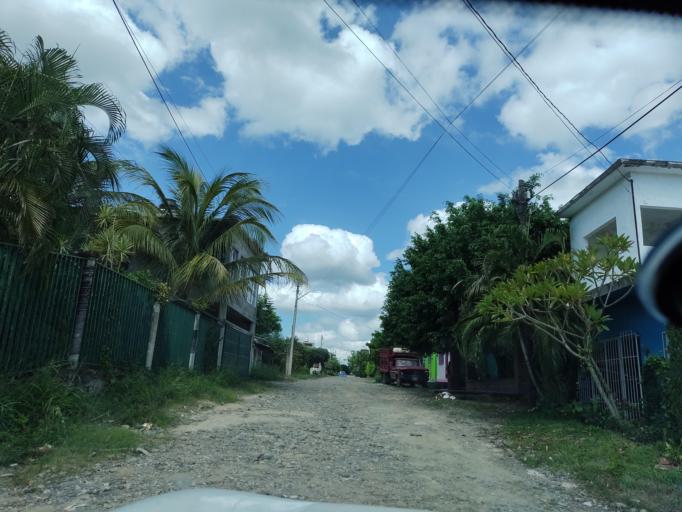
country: MX
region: Veracruz
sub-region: Martinez de la Torre
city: El Progreso
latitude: 20.1145
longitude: -97.0119
